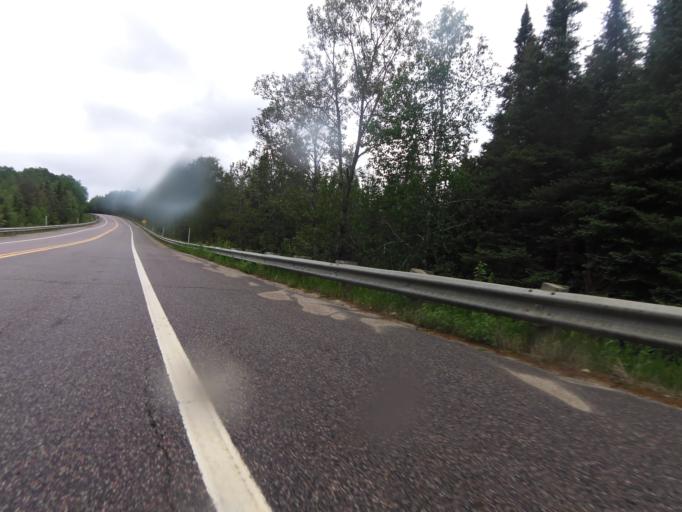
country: CA
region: Quebec
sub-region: Outaouais
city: Shawville
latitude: 45.9271
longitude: -76.2377
